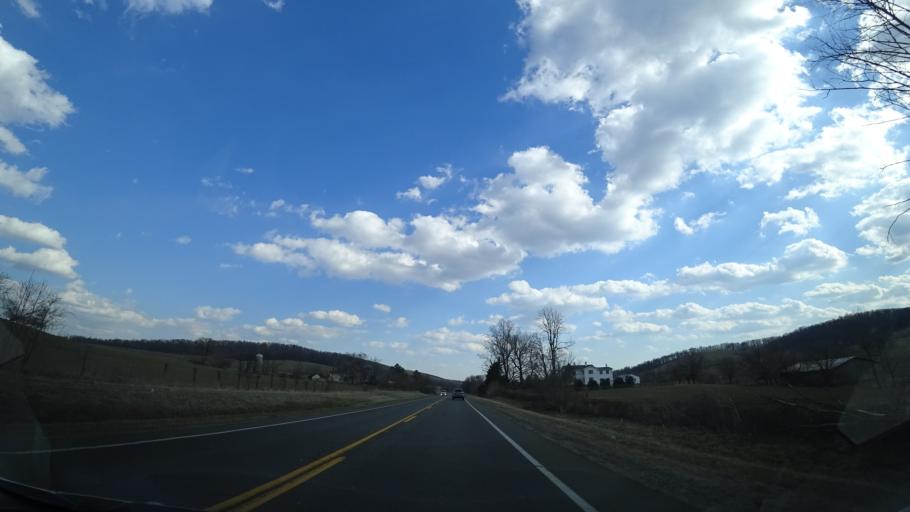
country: US
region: Virginia
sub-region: Warren County
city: Shenandoah Farms
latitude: 38.9672
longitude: -77.9492
